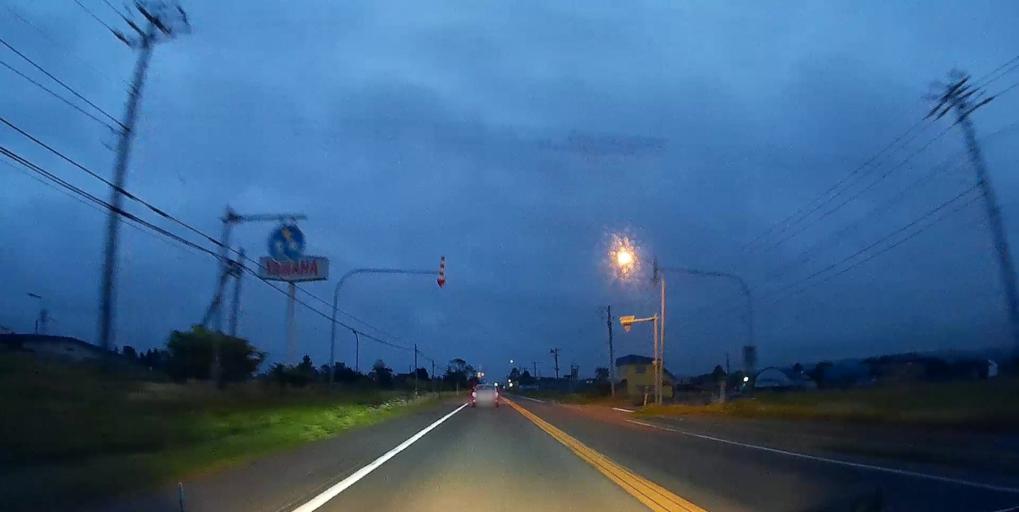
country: JP
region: Hokkaido
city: Nanae
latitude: 42.2205
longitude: 140.3749
